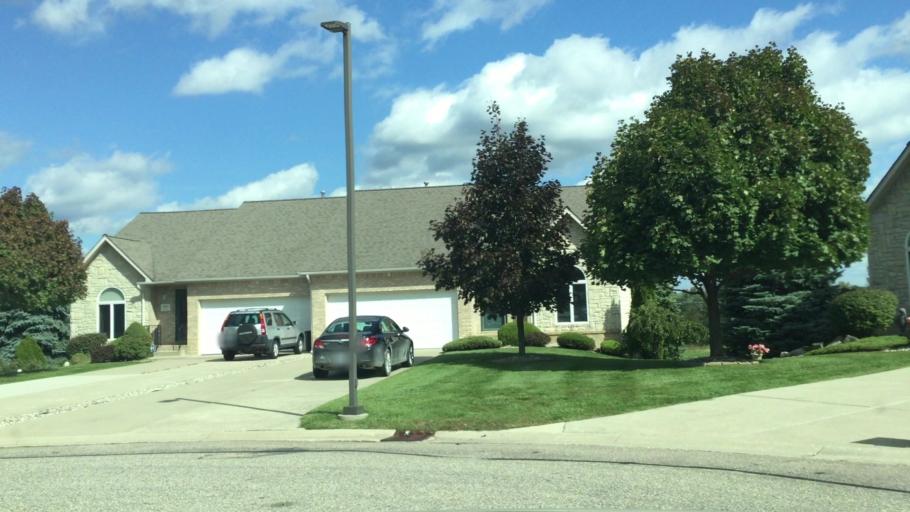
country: US
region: Michigan
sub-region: Genesee County
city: Grand Blanc
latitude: 42.9426
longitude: -83.6036
